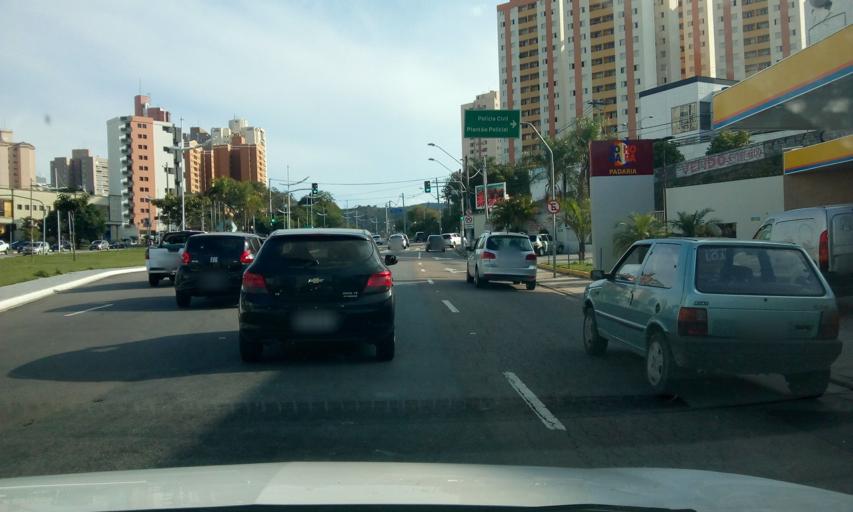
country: BR
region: Sao Paulo
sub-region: Jundiai
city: Jundiai
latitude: -23.2025
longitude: -46.8927
